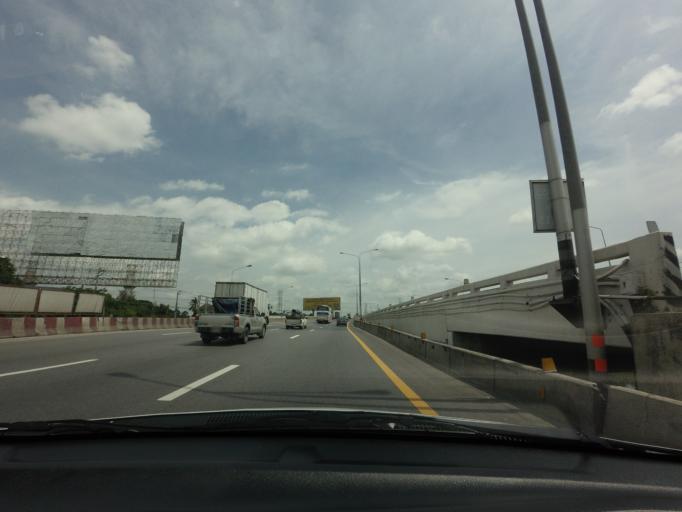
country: TH
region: Bangkok
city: Saphan Sung
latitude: 13.7512
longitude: 100.7017
